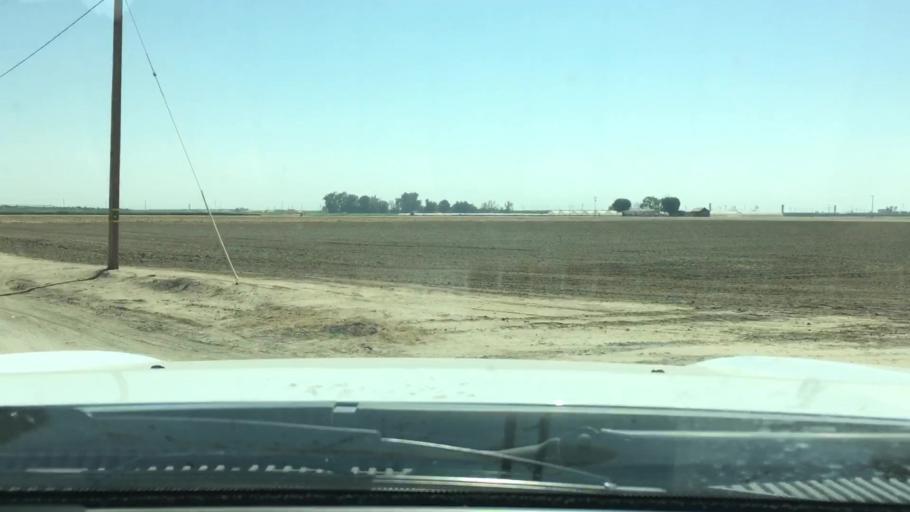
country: US
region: California
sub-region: Kern County
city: Shafter
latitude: 35.5364
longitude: -119.2777
